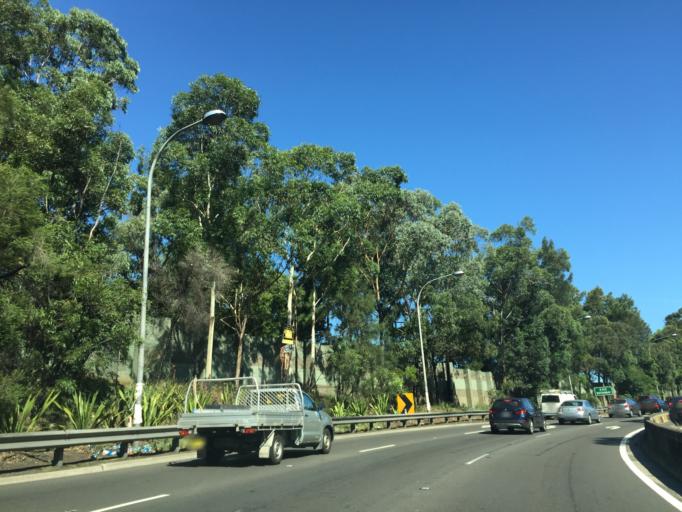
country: AU
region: New South Wales
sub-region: Strathfield
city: Homebush
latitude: -33.8657
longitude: 151.0946
